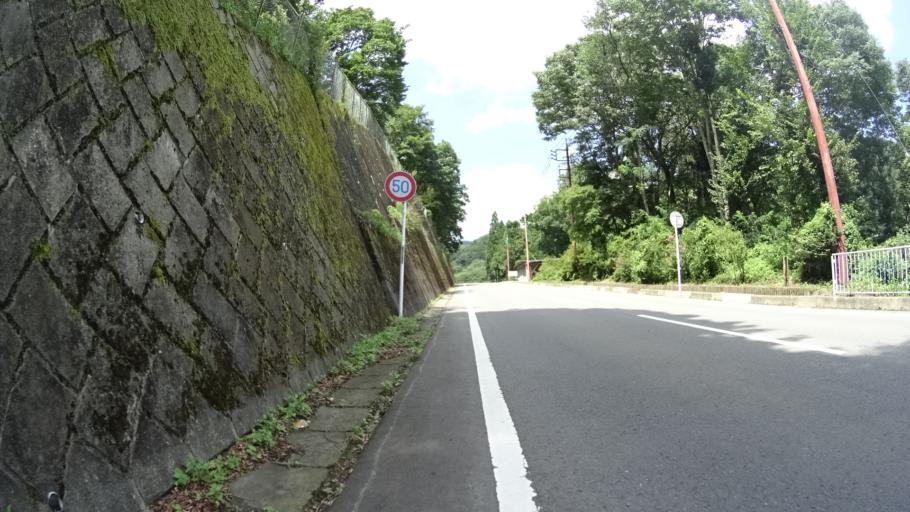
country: JP
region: Gunma
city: Tomioka
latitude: 36.0829
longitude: 138.7512
